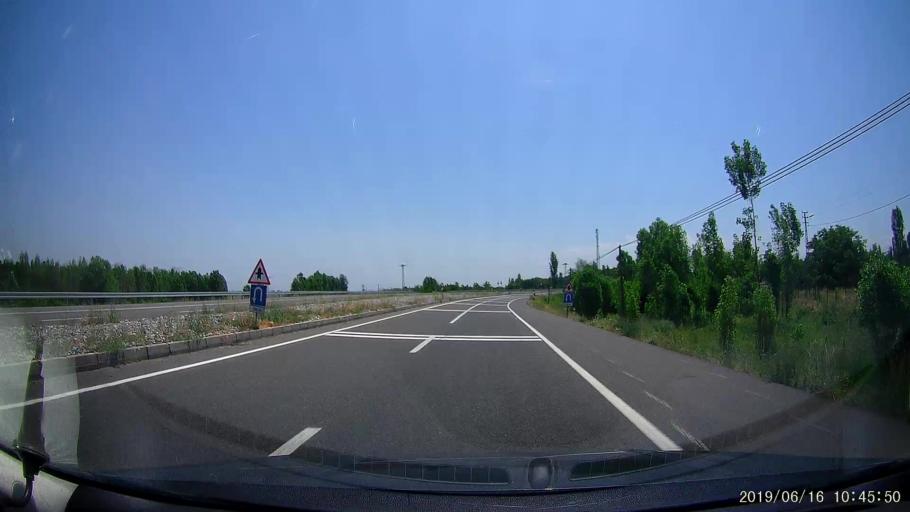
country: AM
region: Armavir
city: Shenavan
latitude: 40.0261
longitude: 43.8742
